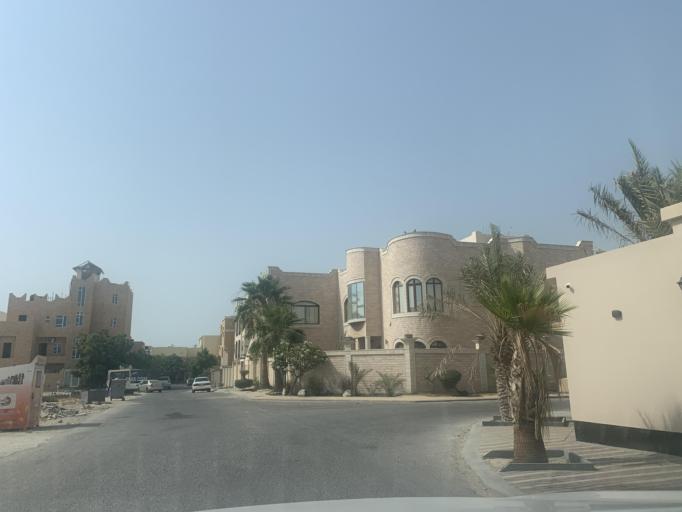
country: BH
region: Manama
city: Jidd Hafs
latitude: 26.2196
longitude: 50.4720
